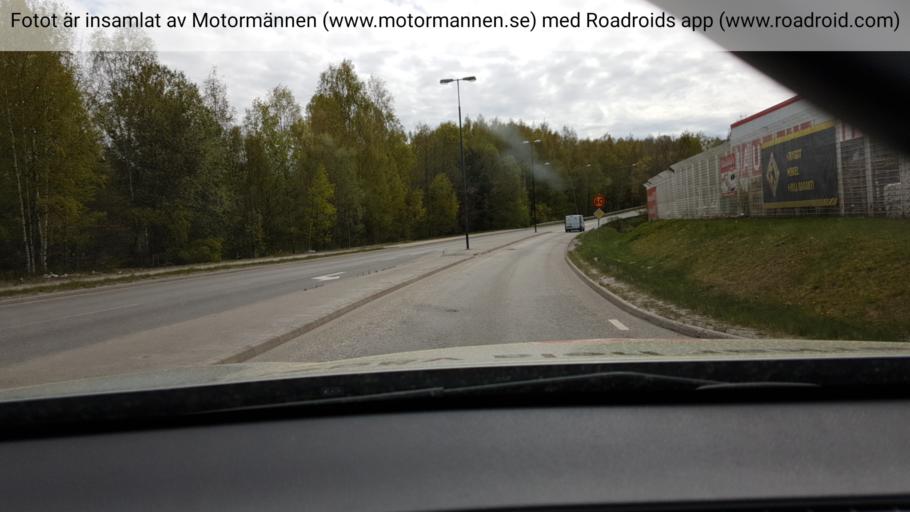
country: SE
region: Stockholm
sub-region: Haninge Kommun
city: Handen
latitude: 59.1985
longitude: 18.1387
